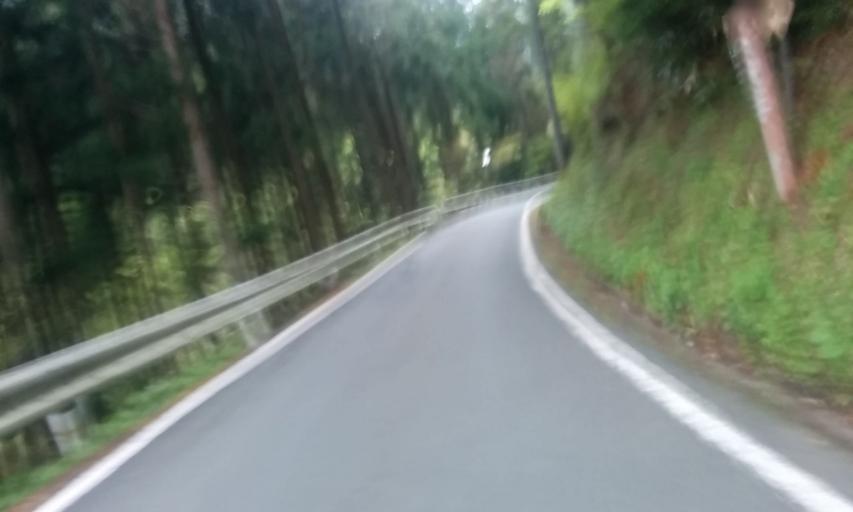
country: JP
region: Ehime
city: Saijo
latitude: 33.7988
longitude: 133.2843
